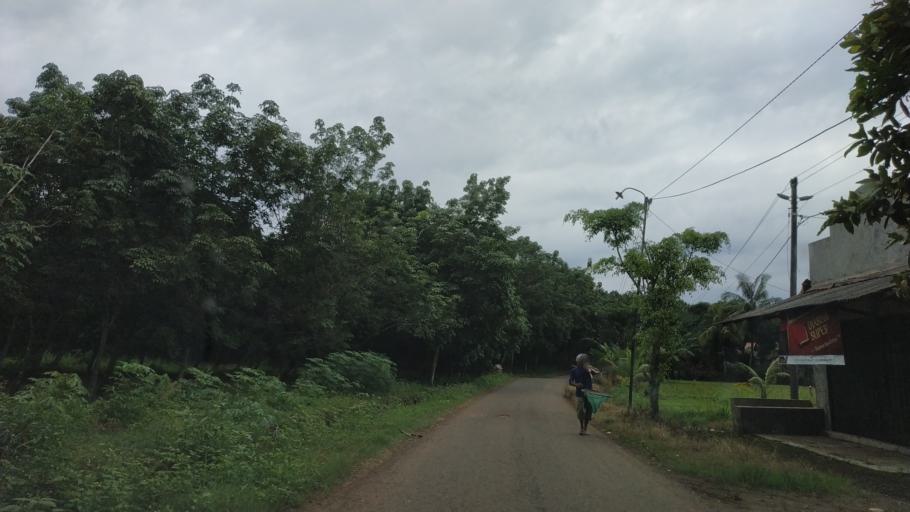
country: ID
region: Central Java
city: Krajan Tegalombo
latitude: -6.4398
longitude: 110.9817
